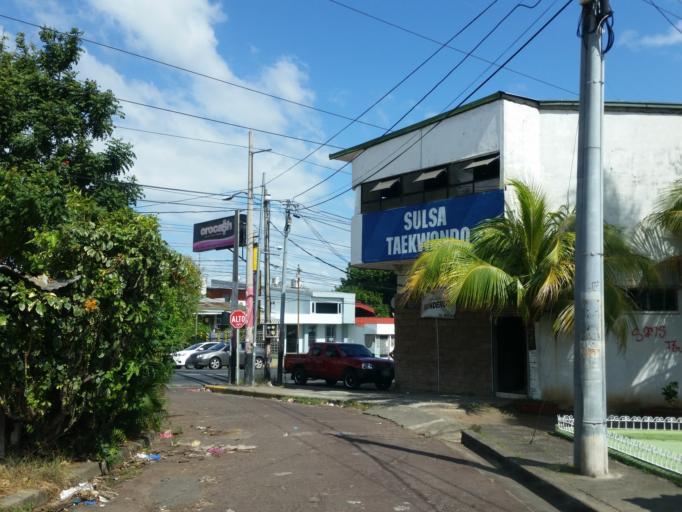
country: NI
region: Managua
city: Managua
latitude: 12.1149
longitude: -86.2534
